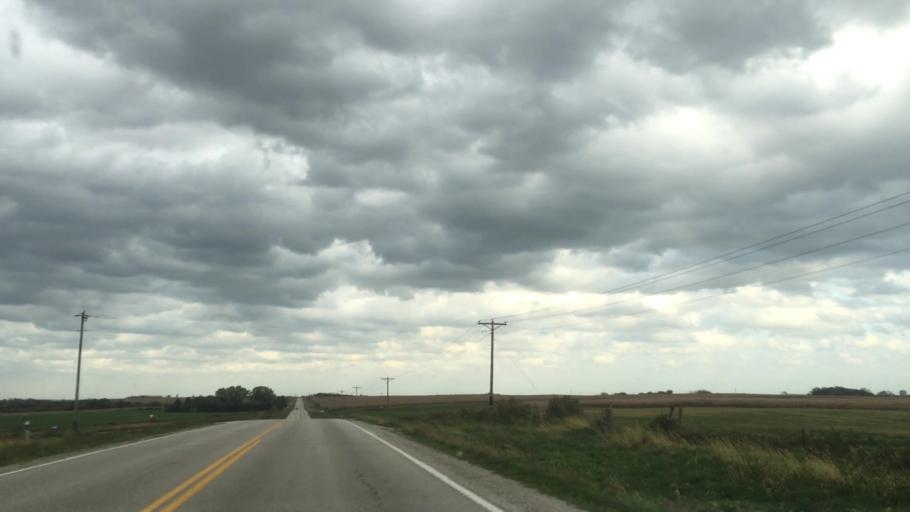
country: US
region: Minnesota
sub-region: Fillmore County
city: Preston
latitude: 43.7318
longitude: -92.0801
